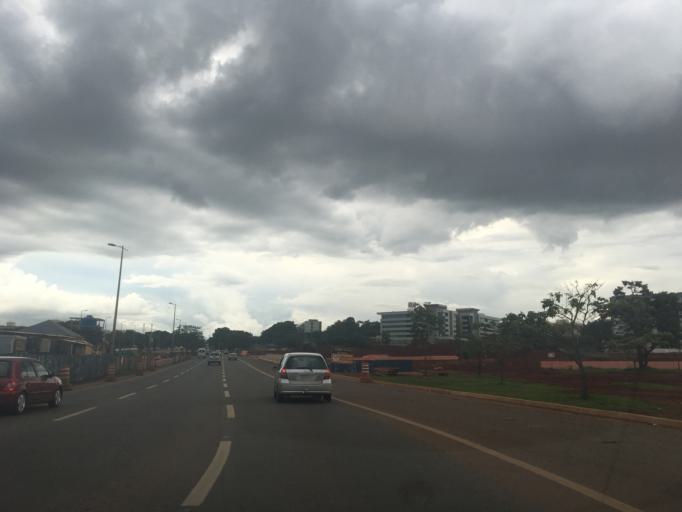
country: BR
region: Federal District
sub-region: Brasilia
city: Brasilia
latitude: -15.7326
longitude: -47.8939
